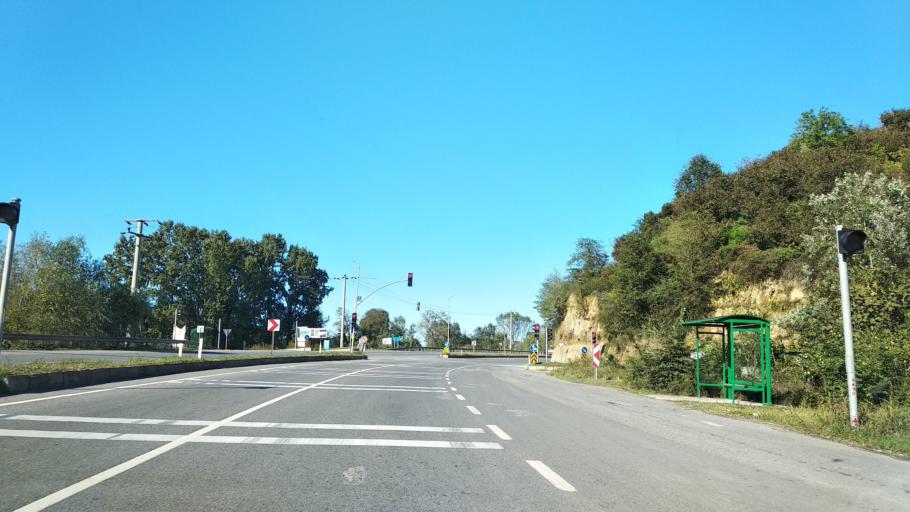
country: TR
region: Sakarya
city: Karasu
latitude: 41.0800
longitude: 30.6459
